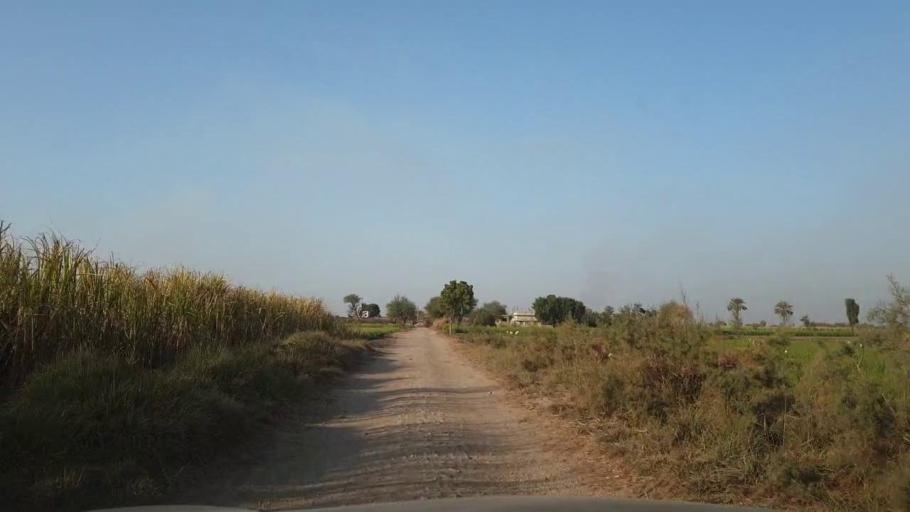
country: PK
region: Sindh
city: Tando Allahyar
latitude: 25.5944
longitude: 68.6822
